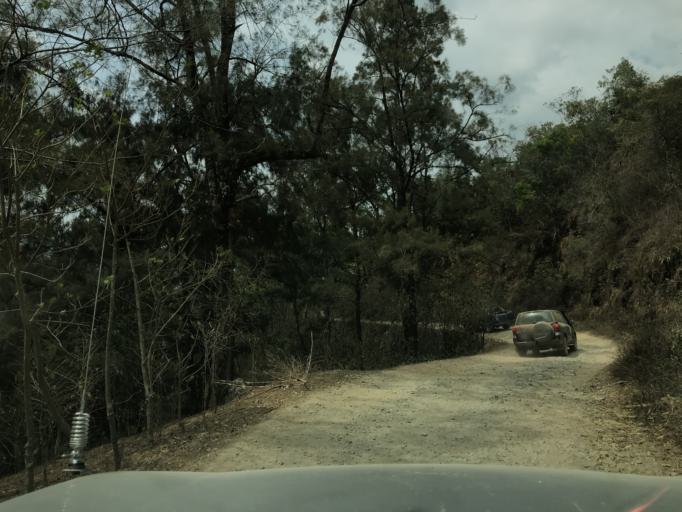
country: TL
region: Ermera
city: Gleno
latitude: -8.8227
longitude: 125.4334
